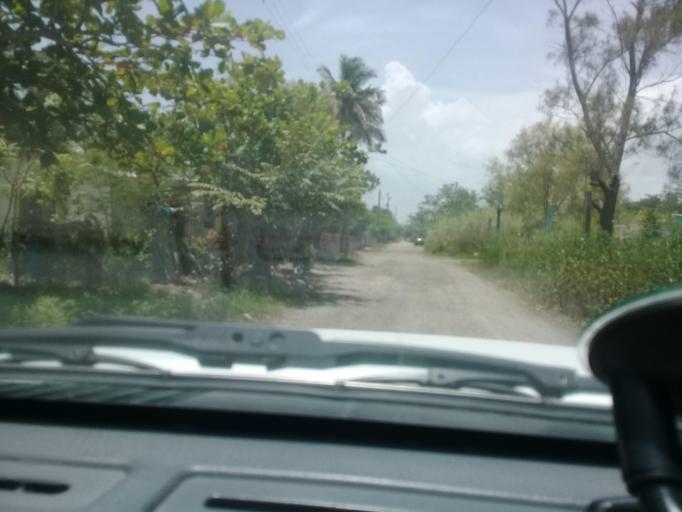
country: MX
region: Veracruz
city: Anahuac
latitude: 22.2278
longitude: -97.8186
